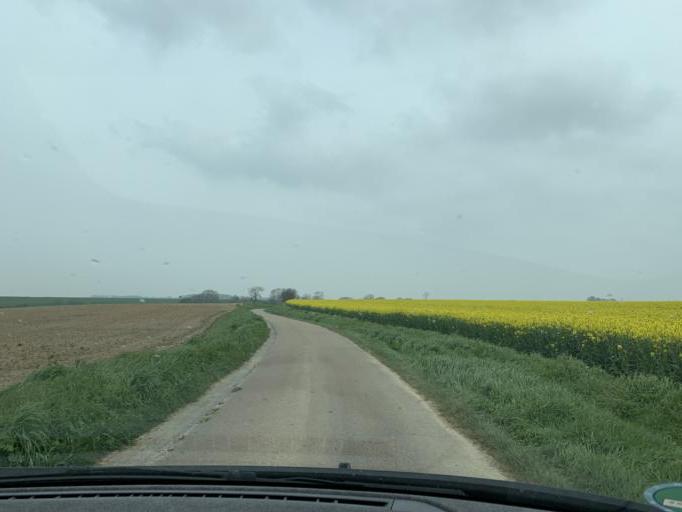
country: FR
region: Haute-Normandie
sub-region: Departement de la Seine-Maritime
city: Fontaine-le-Dun
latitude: 49.8564
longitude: 0.8125
